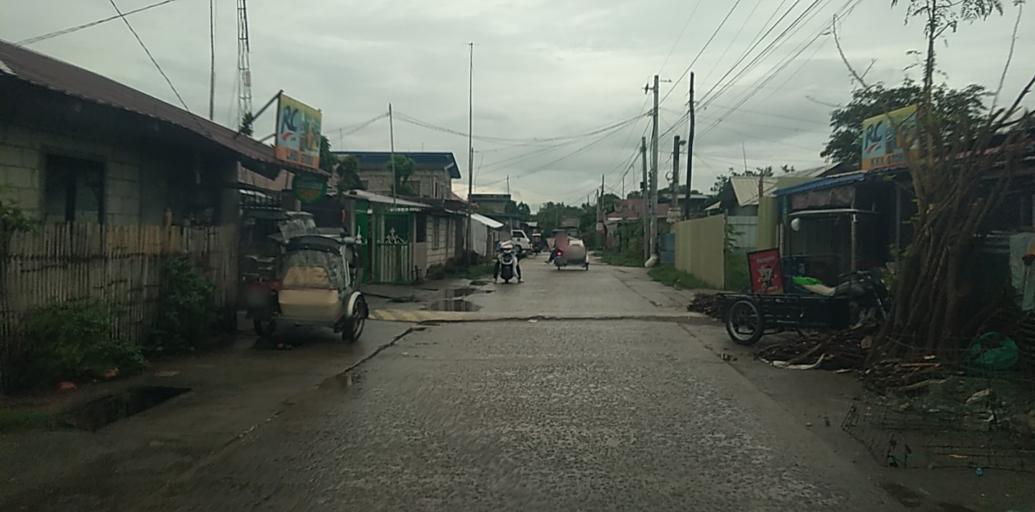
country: PH
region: Central Luzon
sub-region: Province of Pampanga
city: Arayat
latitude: 15.1534
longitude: 120.7403
